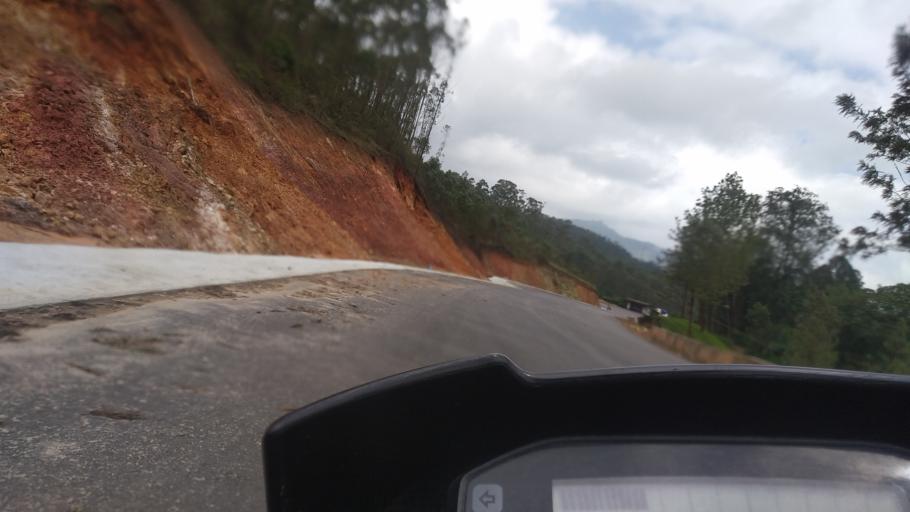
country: IN
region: Kerala
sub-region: Idukki
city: Munnar
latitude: 10.0730
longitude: 77.0913
